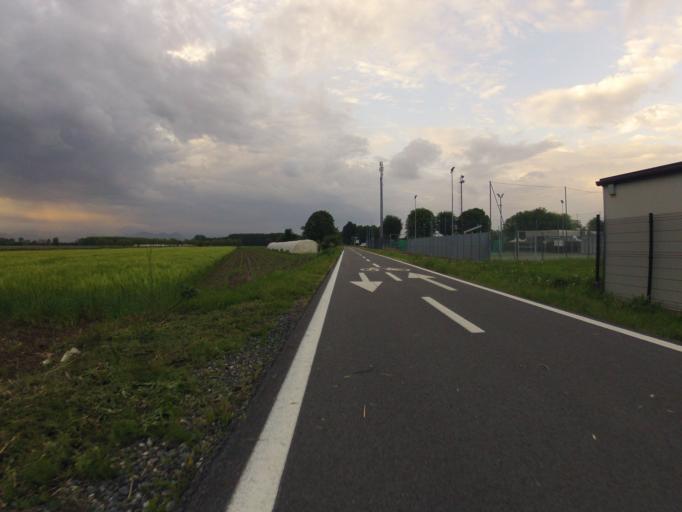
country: IT
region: Piedmont
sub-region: Provincia di Torino
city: Vigone
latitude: 44.8459
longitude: 7.4908
